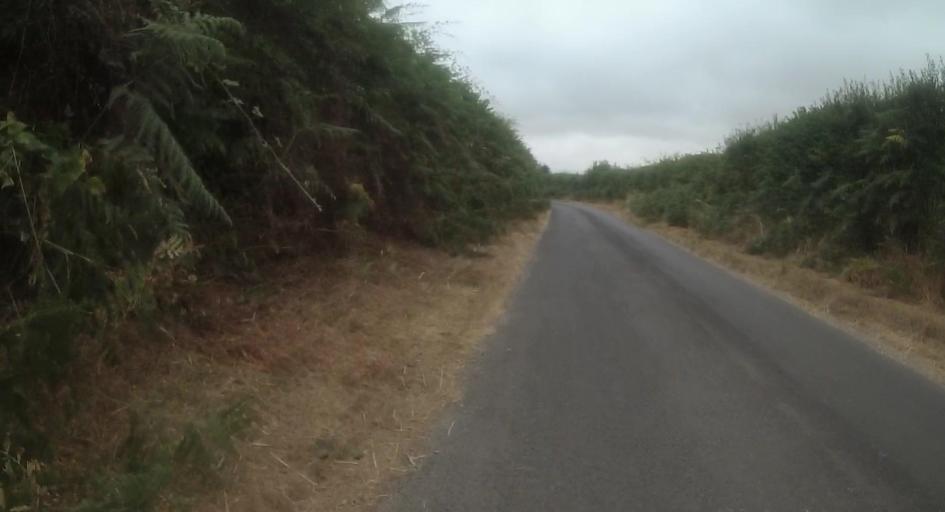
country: GB
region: England
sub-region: Dorset
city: Bovington Camp
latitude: 50.7323
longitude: -2.2050
